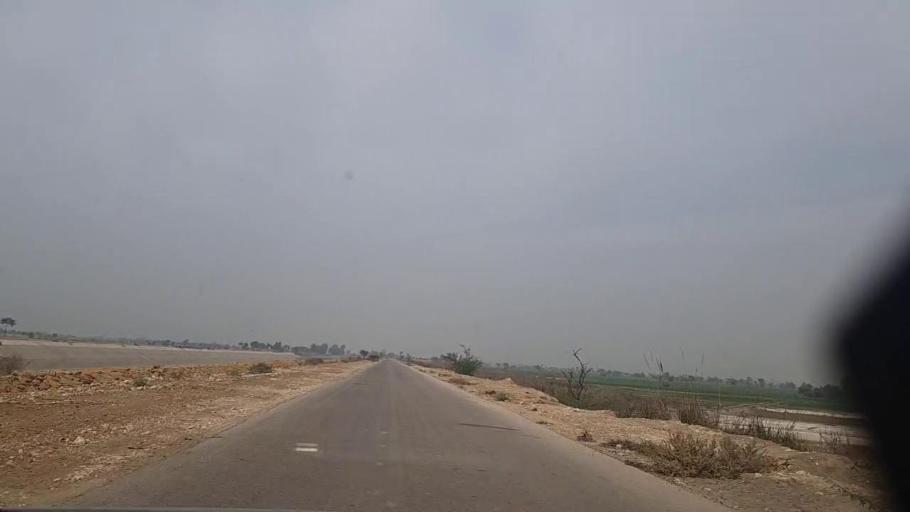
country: PK
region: Sindh
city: Sakrand
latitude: 26.2754
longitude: 68.2316
